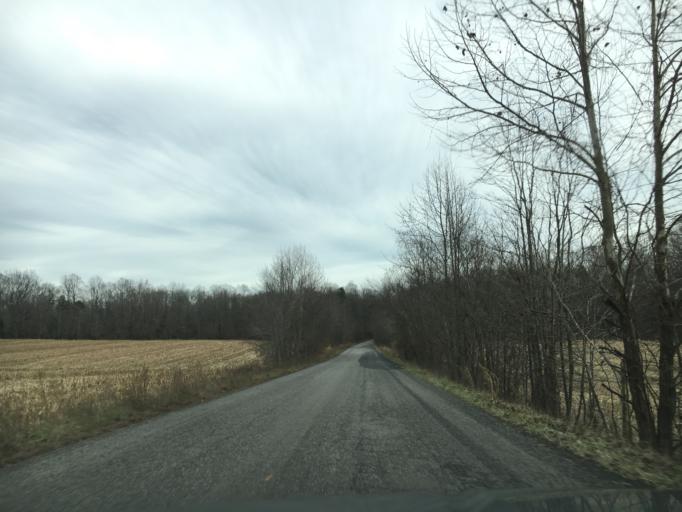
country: US
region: Virginia
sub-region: Amelia County
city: Amelia Court House
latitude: 37.4256
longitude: -78.0036
